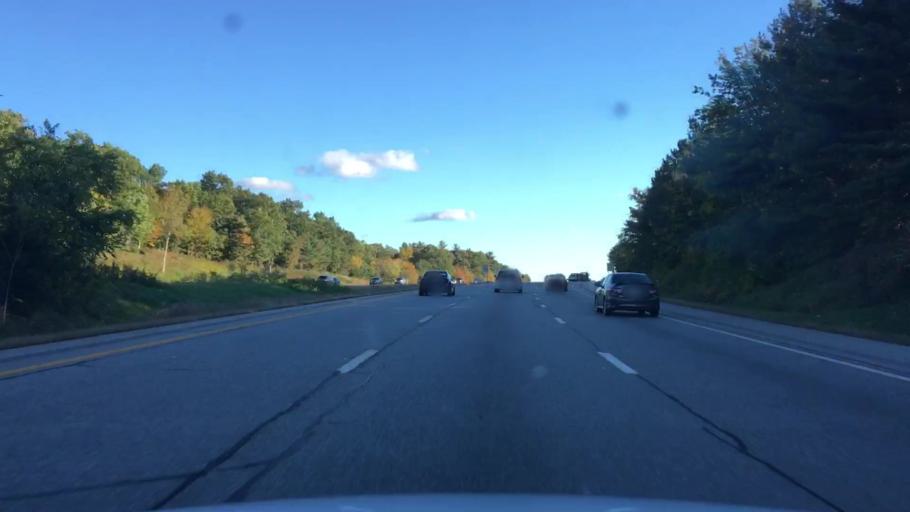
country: US
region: New Hampshire
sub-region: Merrimack County
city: South Hooksett
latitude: 43.0110
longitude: -71.4348
